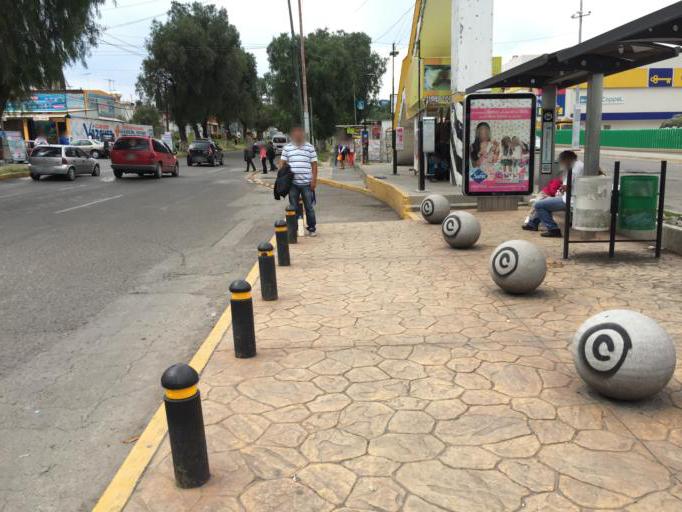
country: MX
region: Mexico
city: Cuautitlan Izcalli
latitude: 19.6468
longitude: -99.2082
